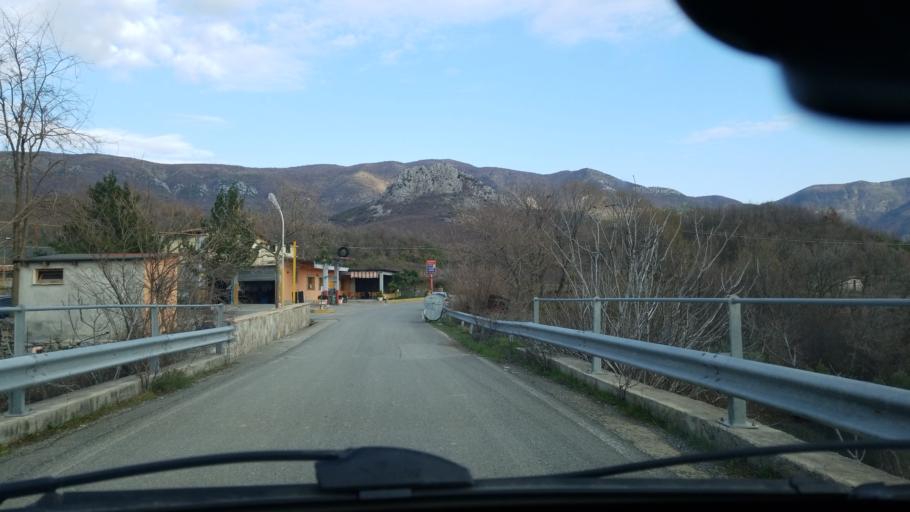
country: AL
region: Lezhe
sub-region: Rrethi i Lezhes
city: Kallmeti i Madh
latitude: 41.8835
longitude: 19.6898
